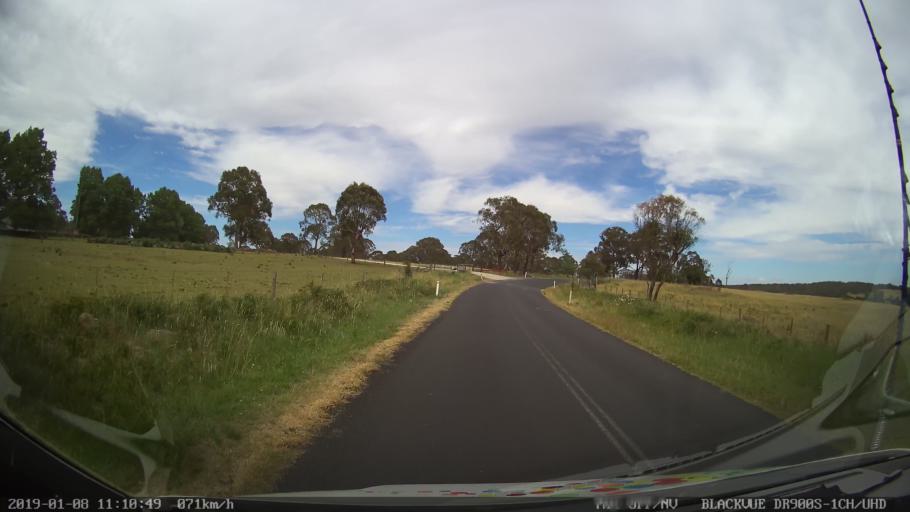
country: AU
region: New South Wales
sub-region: Guyra
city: Guyra
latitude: -30.2264
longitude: 151.6319
